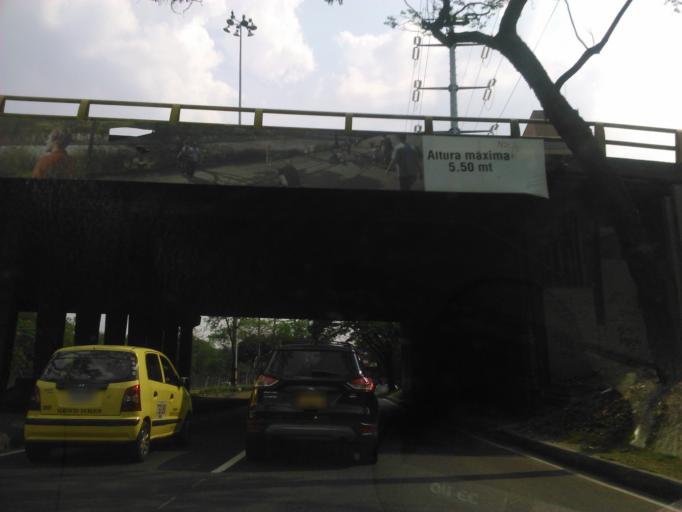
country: CO
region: Antioquia
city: Medellin
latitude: 6.2547
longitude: -75.5775
